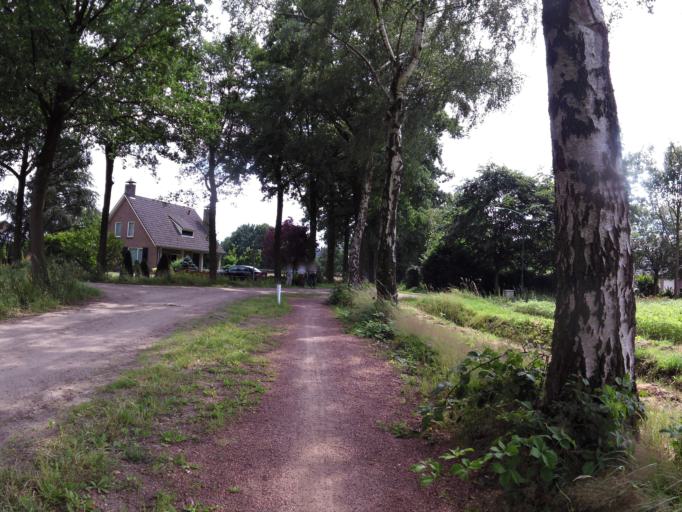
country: NL
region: North Brabant
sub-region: Gemeente Sint-Oedenrode
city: Sint-Oedenrode
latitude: 51.5782
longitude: 5.4676
